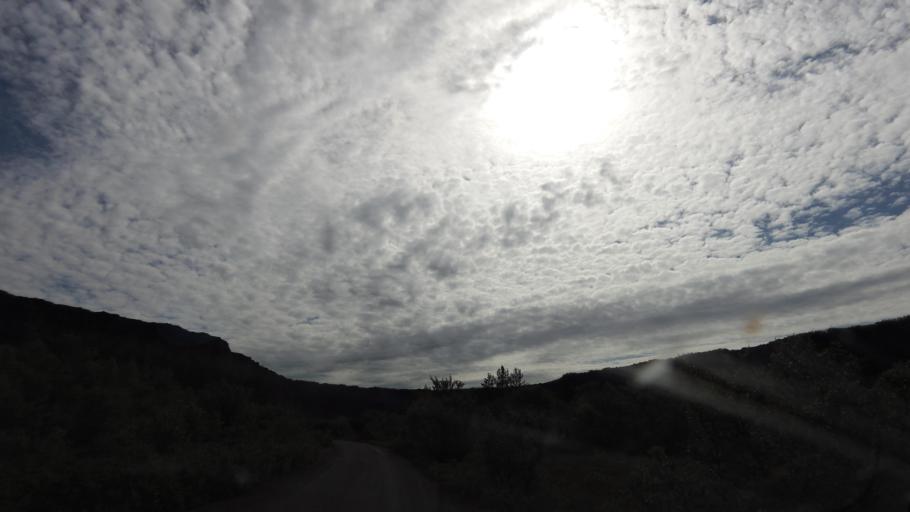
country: IS
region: Northeast
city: Husavik
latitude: 66.0057
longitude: -16.5101
